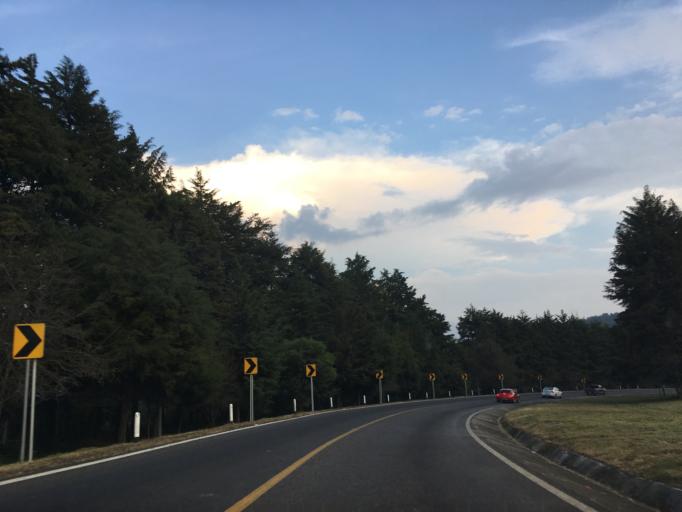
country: MX
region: Michoacan
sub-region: Patzcuaro
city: Santa Maria Huiramangaro (San Juan Tumbio)
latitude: 19.4896
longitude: -101.7390
